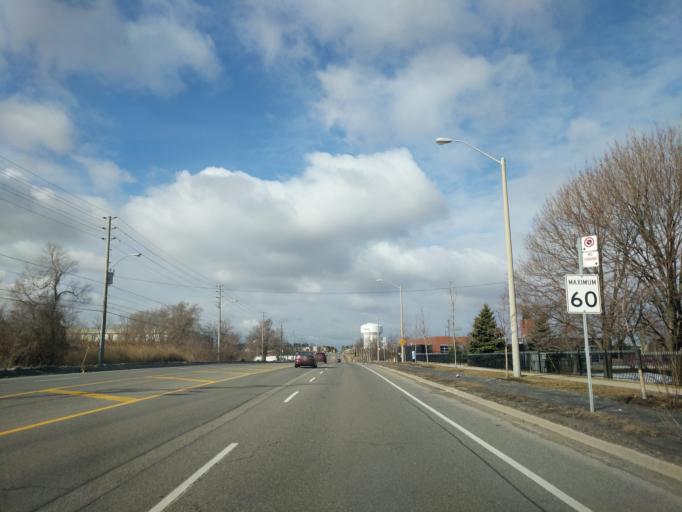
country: CA
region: Ontario
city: Scarborough
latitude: 43.8049
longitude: -79.1873
